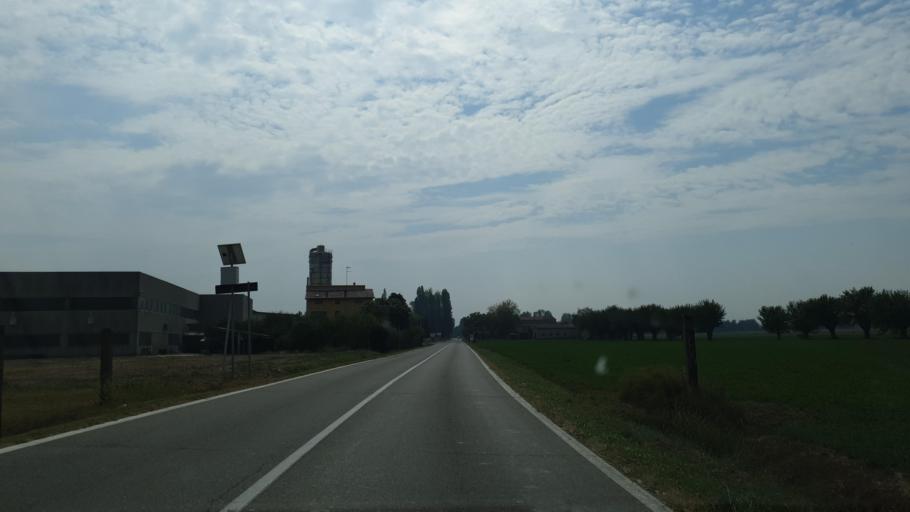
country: IT
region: Emilia-Romagna
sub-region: Provincia di Parma
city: San Secondo Parmense
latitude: 44.8818
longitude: 10.2558
